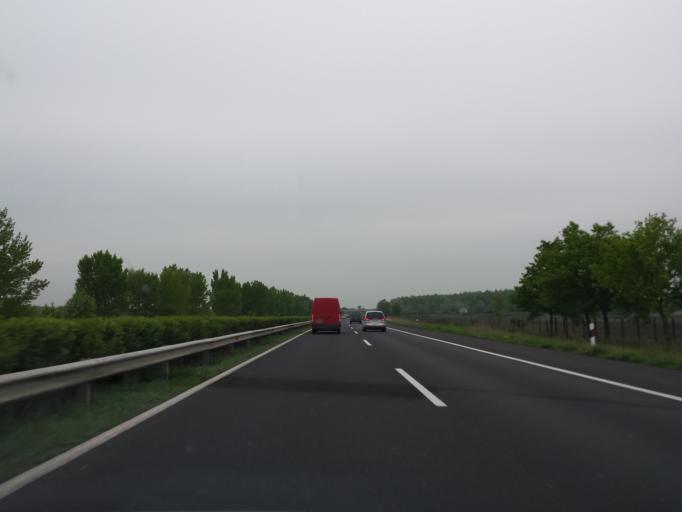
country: HU
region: Gyor-Moson-Sopron
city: Kimle
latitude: 47.8030
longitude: 17.3055
